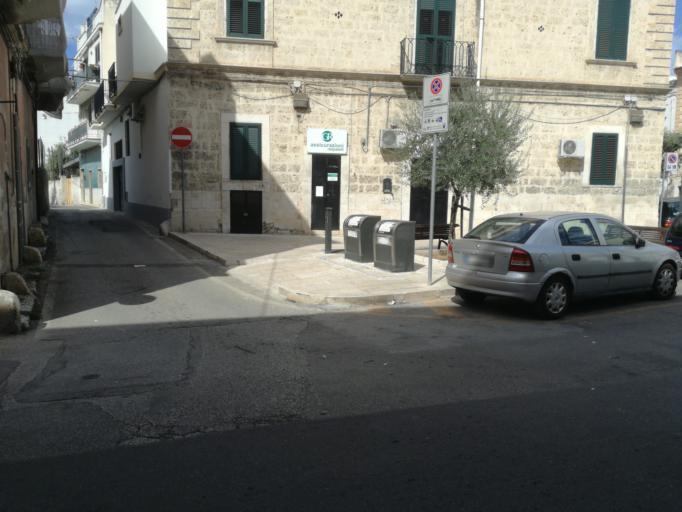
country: IT
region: Apulia
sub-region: Provincia di Bari
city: Triggiano
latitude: 41.0634
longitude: 16.9202
